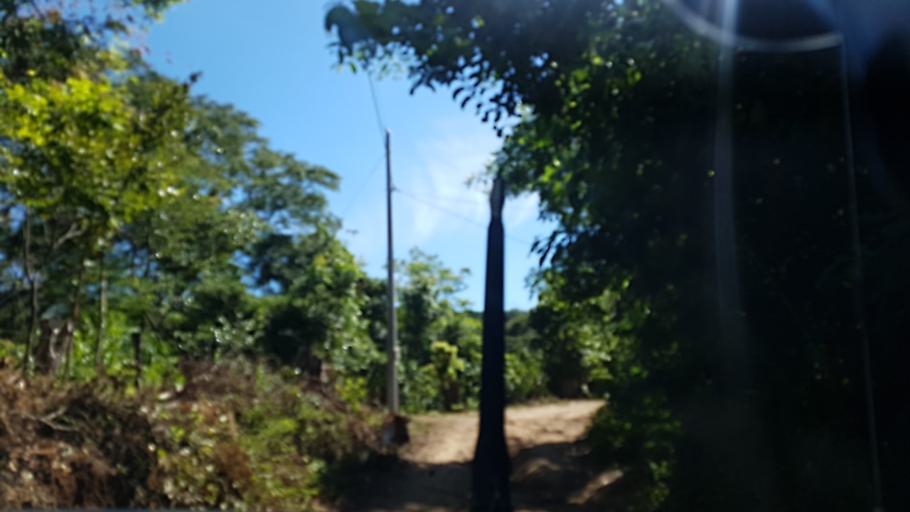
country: NI
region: Carazo
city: Santa Teresa
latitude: 11.6684
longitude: -86.1736
